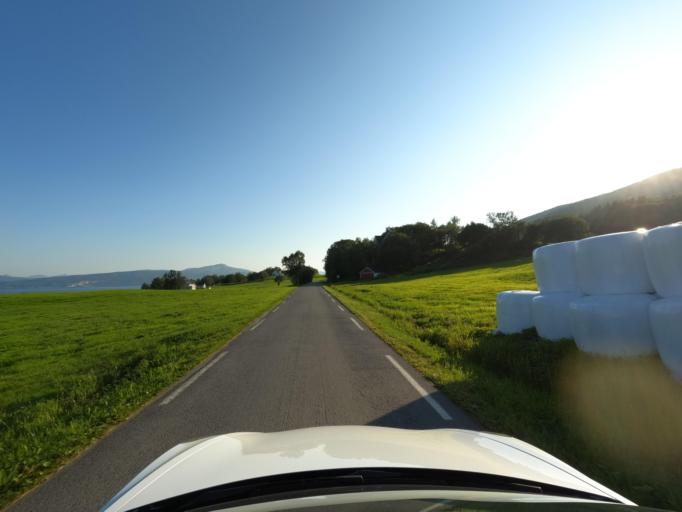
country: NO
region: Nordland
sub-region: Evenes
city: Randa
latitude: 68.4738
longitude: 16.8784
